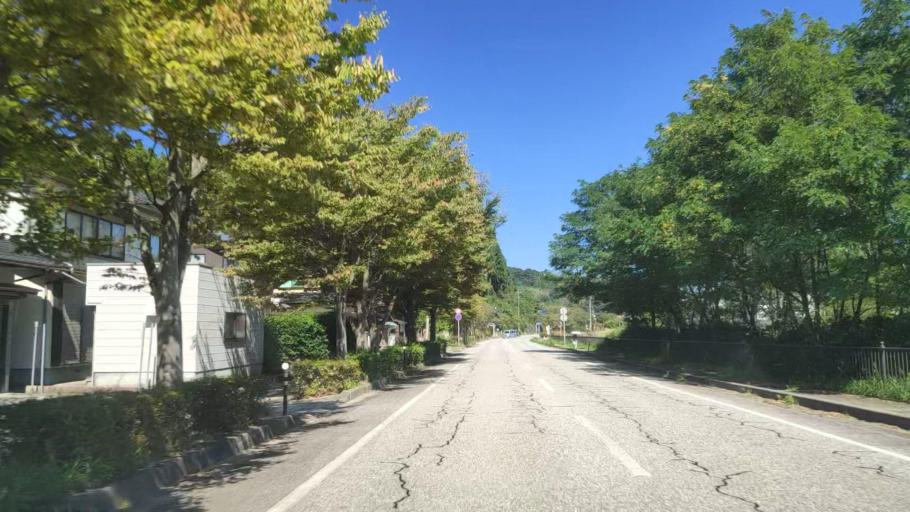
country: JP
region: Ishikawa
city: Nanao
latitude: 37.3903
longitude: 136.8927
